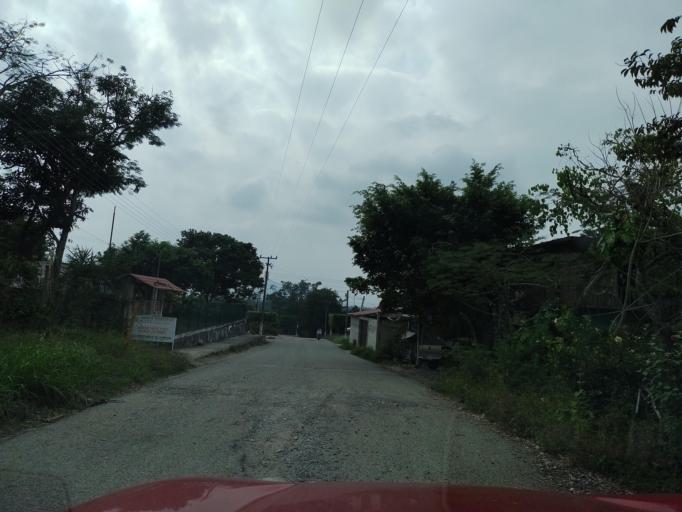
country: MX
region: Veracruz
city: Agua Dulce
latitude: 20.3425
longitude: -97.2923
